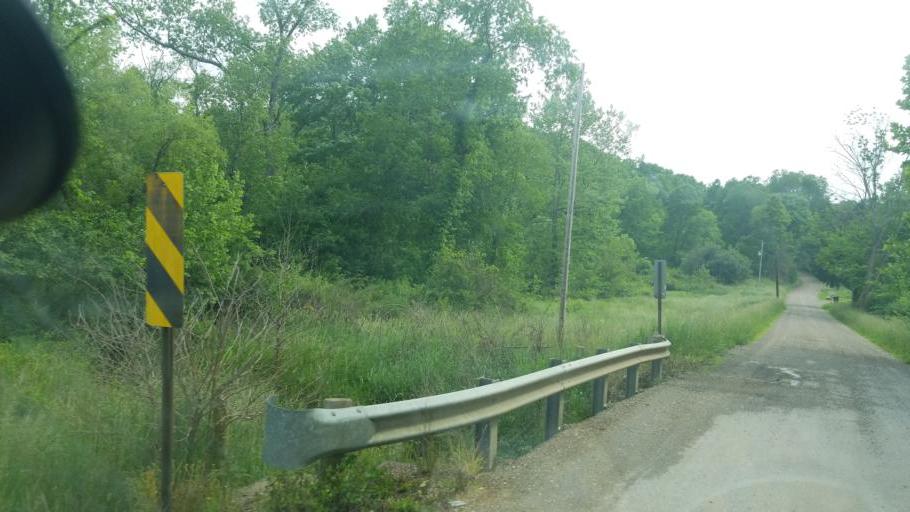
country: US
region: Ohio
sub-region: Muskingum County
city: Frazeysburg
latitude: 40.2626
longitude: -82.1680
